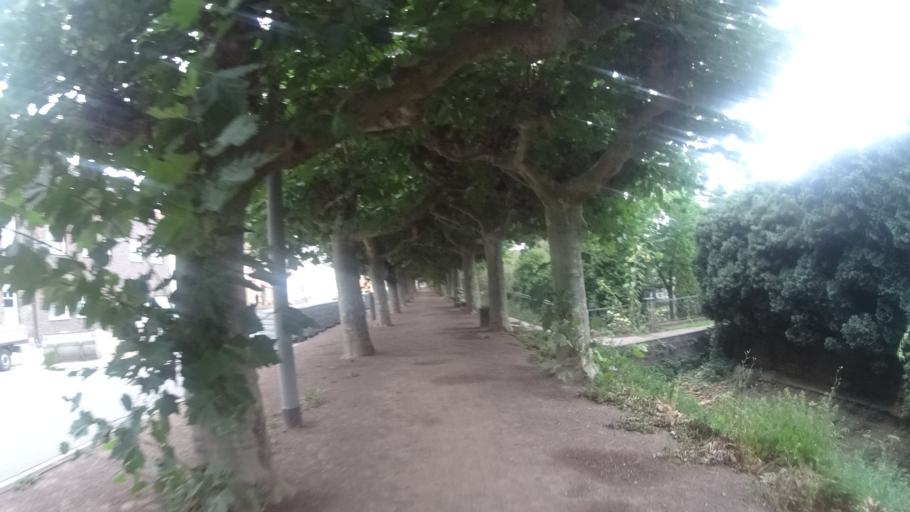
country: DE
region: North Rhine-Westphalia
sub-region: Regierungsbezirk Dusseldorf
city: Wesel
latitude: 51.6275
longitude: 6.5791
